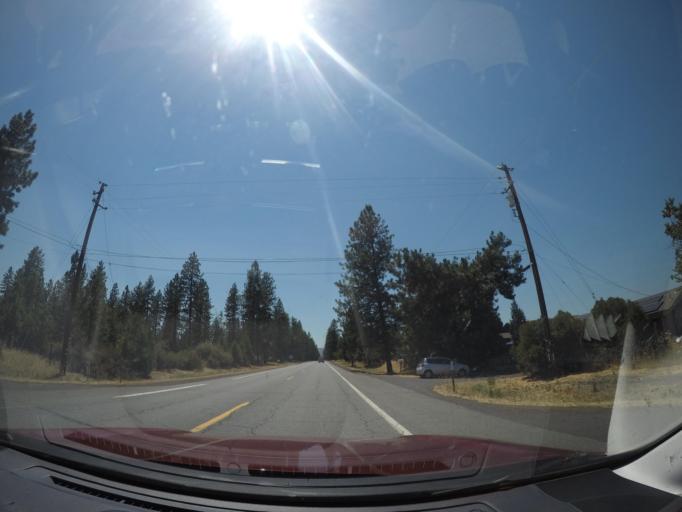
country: US
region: California
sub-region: Shasta County
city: Burney
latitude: 41.0654
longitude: -121.3555
